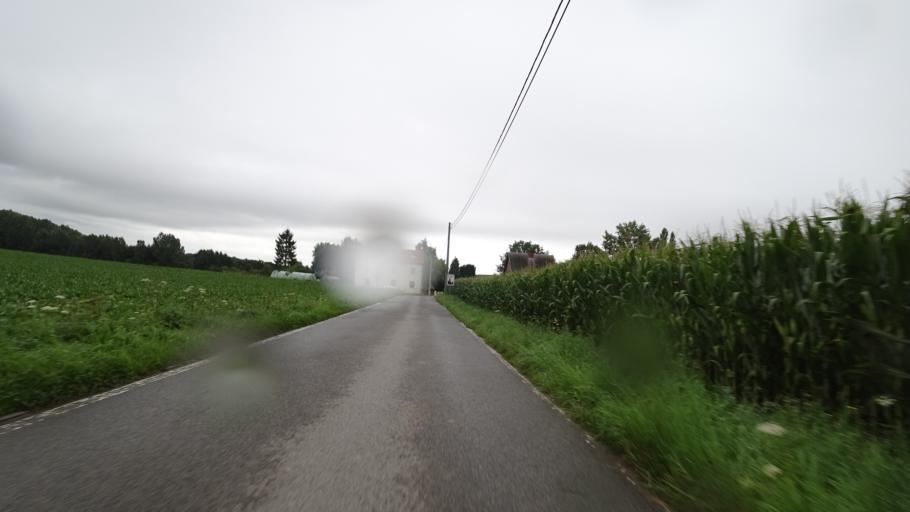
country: BE
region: Wallonia
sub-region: Province de Namur
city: Gembloux
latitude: 50.5618
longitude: 4.7438
